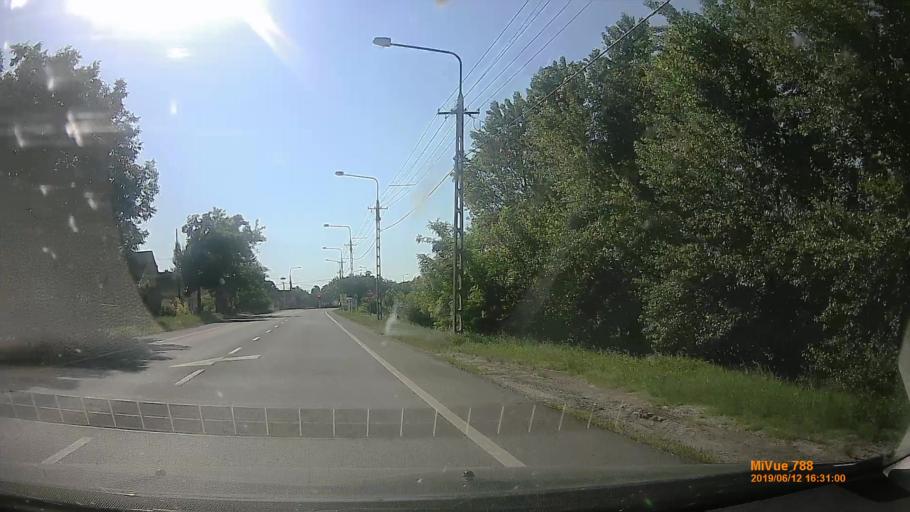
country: HU
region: Csongrad
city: Apatfalva
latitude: 46.1746
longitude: 20.5787
